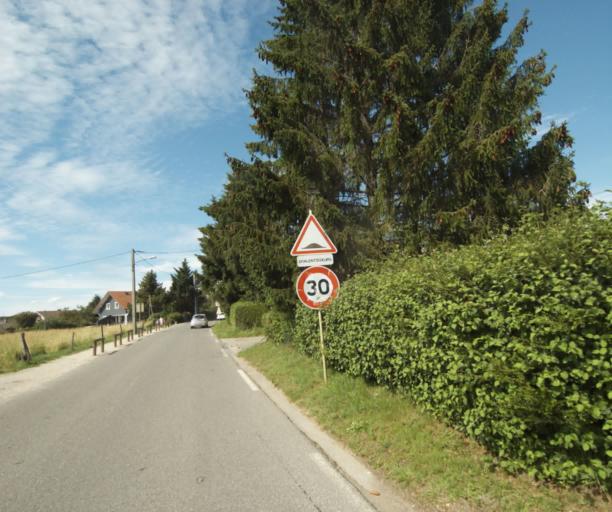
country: FR
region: Rhone-Alpes
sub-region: Departement de la Haute-Savoie
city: Allinges
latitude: 46.3392
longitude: 6.4802
